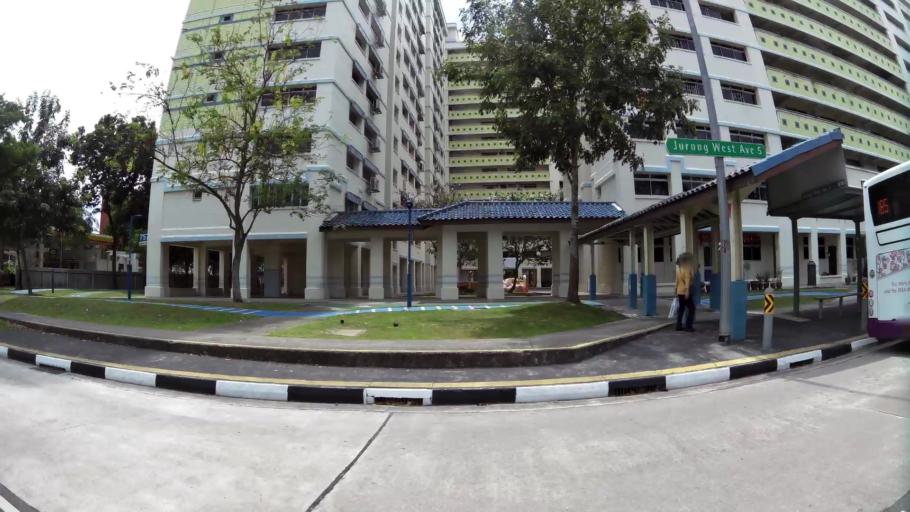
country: MY
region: Johor
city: Johor Bahru
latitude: 1.3504
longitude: 103.7007
